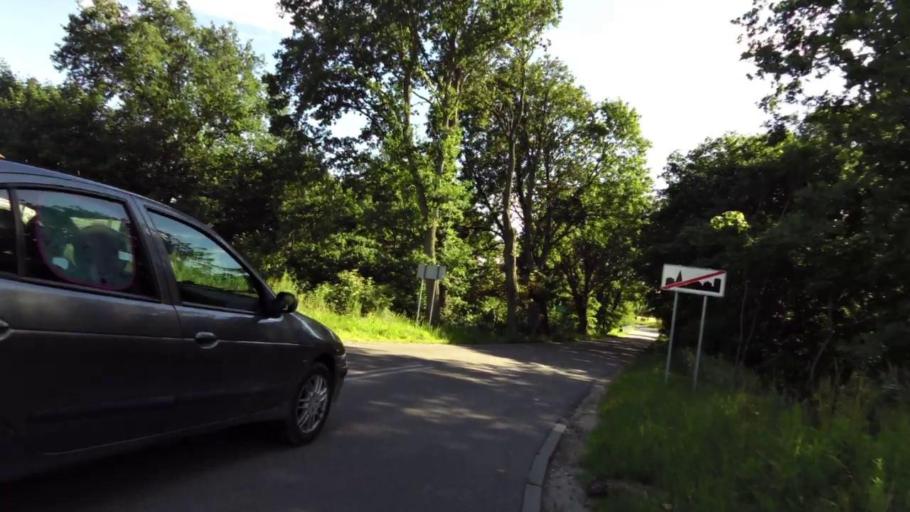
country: PL
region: West Pomeranian Voivodeship
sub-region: Powiat slawienski
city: Slawno
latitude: 54.4544
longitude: 16.7408
